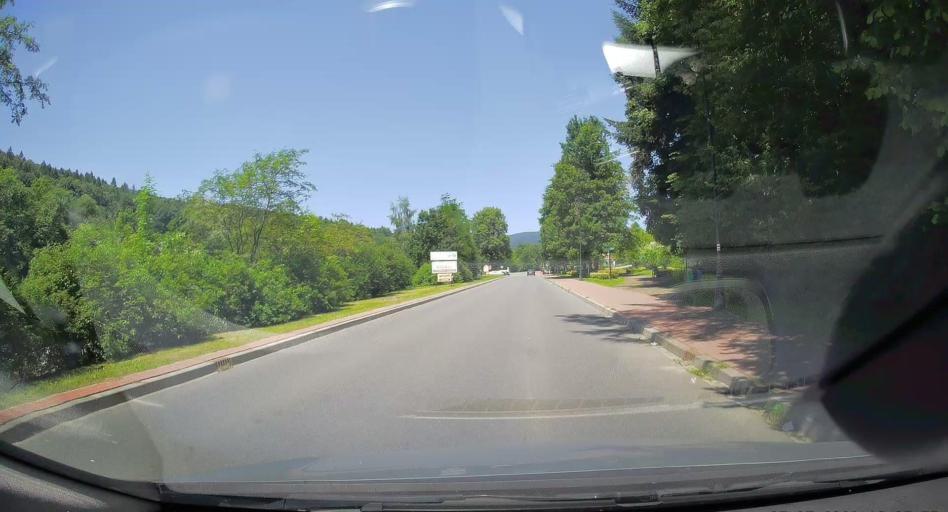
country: PL
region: Lesser Poland Voivodeship
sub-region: Powiat nowosadecki
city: Muszyna
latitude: 49.3544
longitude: 20.8884
